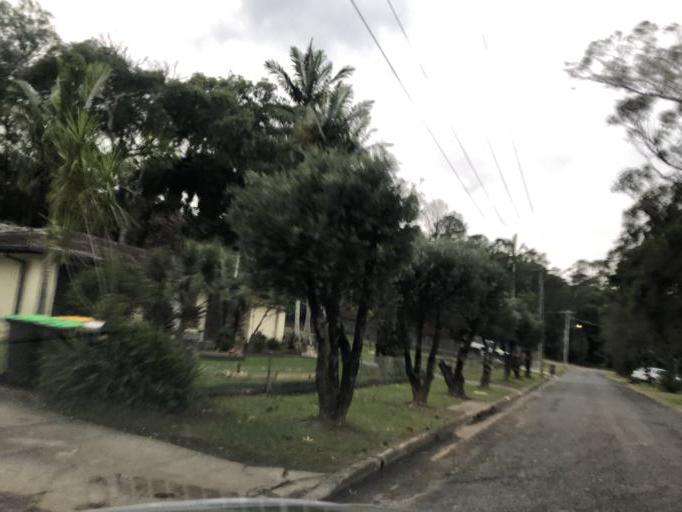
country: AU
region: New South Wales
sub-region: Coffs Harbour
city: Coffs Harbour
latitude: -30.3082
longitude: 153.1278
